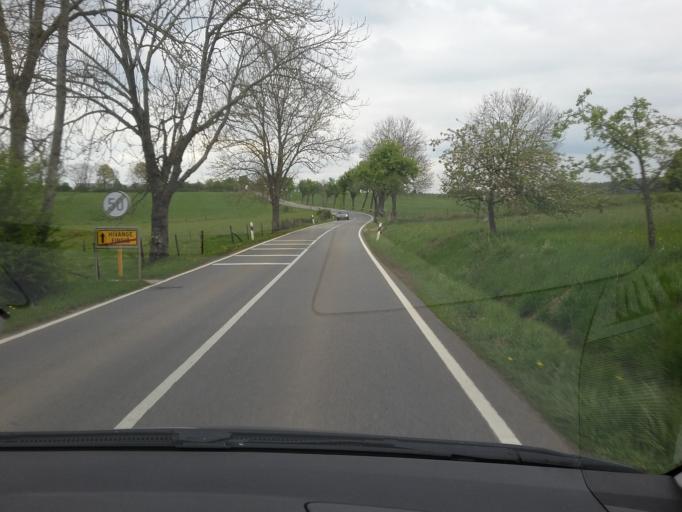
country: LU
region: Luxembourg
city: Hautcharage
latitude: 49.6033
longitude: 5.9127
